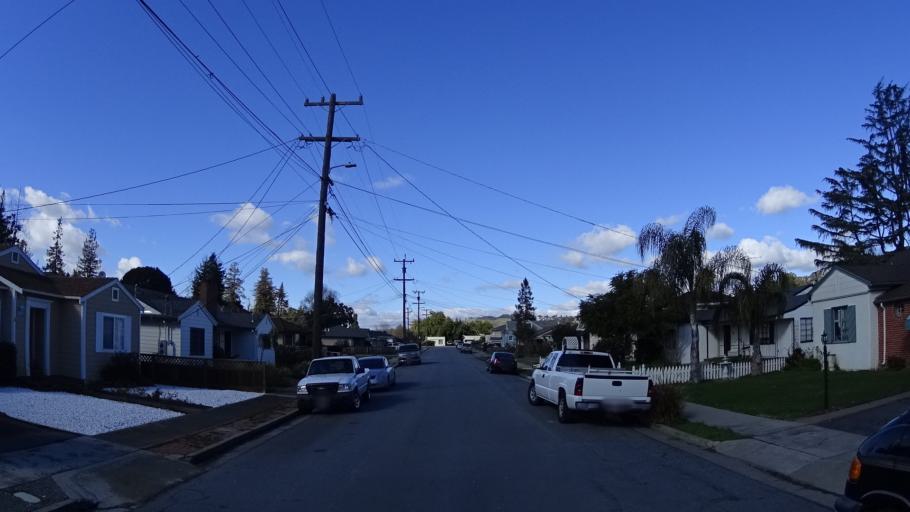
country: US
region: California
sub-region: Alameda County
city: Cherryland
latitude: 37.6838
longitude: -122.1012
